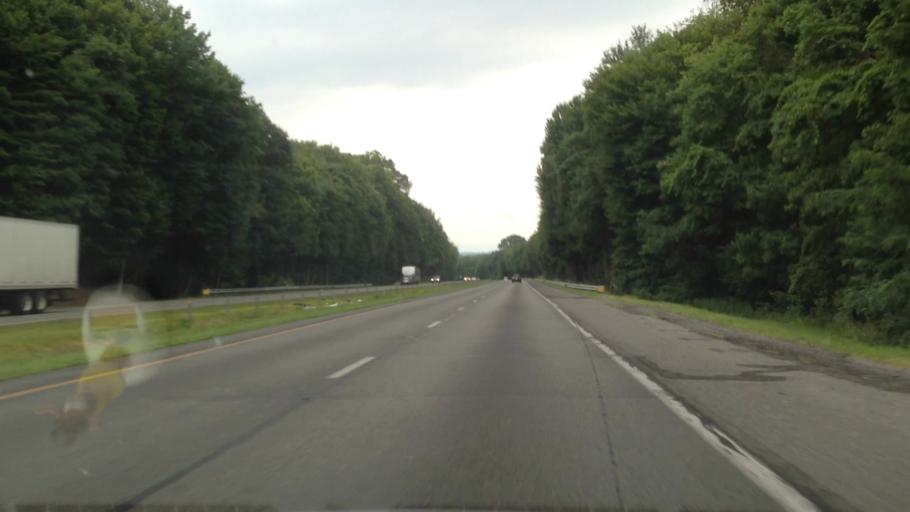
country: US
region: North Carolina
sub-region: Surry County
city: Pilot Mountain
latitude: 36.3515
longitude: -80.4678
